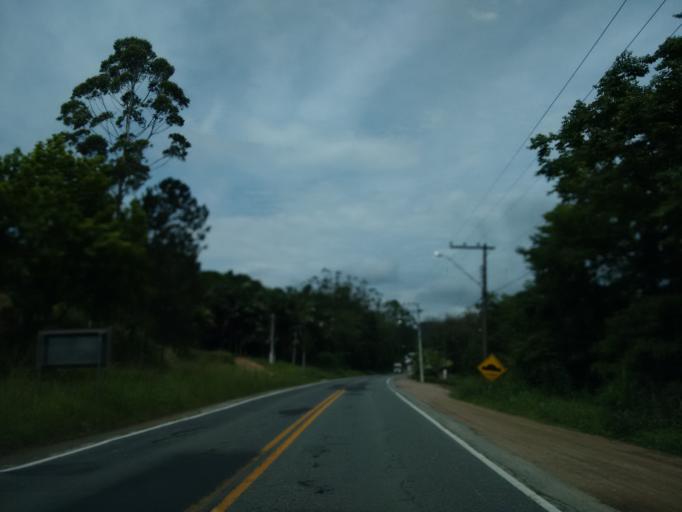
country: BR
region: Santa Catarina
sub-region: Pomerode
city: Pomerode
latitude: -26.6891
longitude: -49.1532
